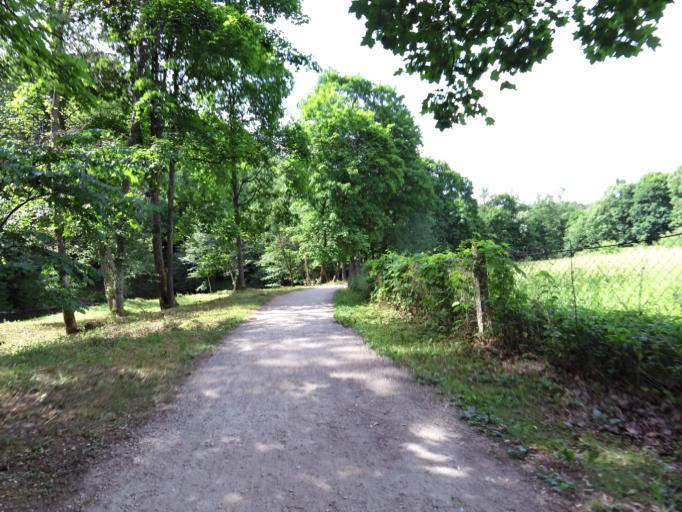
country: LT
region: Vilnius County
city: Rasos
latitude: 54.6870
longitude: 25.3534
